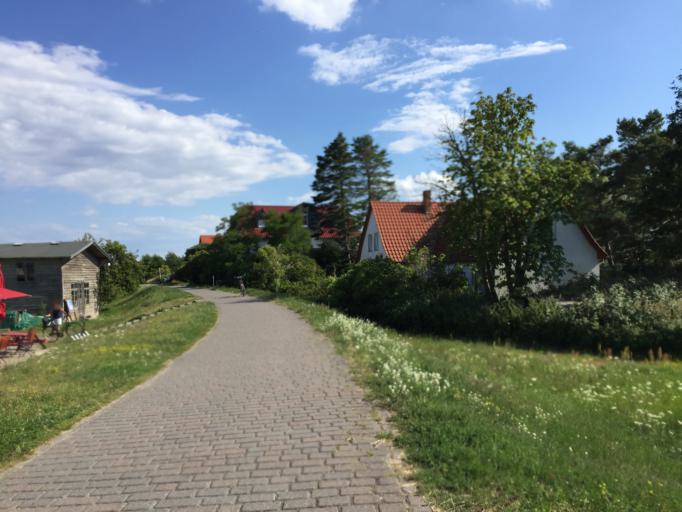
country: DE
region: Mecklenburg-Vorpommern
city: Hiddensee
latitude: 54.5688
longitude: 13.1061
